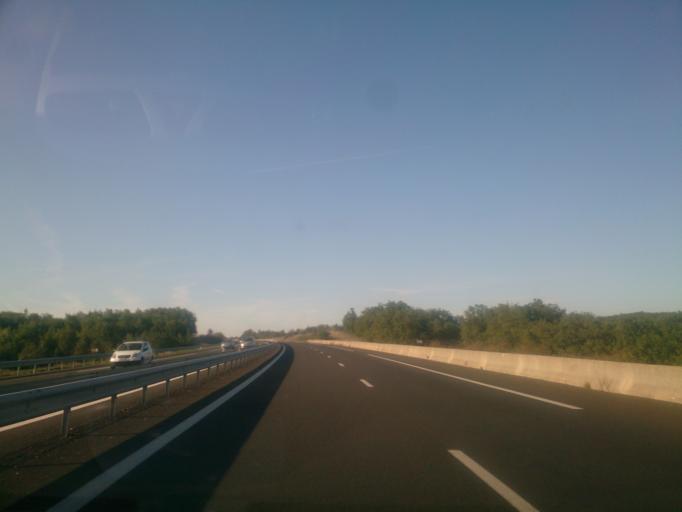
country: FR
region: Midi-Pyrenees
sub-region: Departement du Lot
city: Pradines
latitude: 44.5823
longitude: 1.5153
